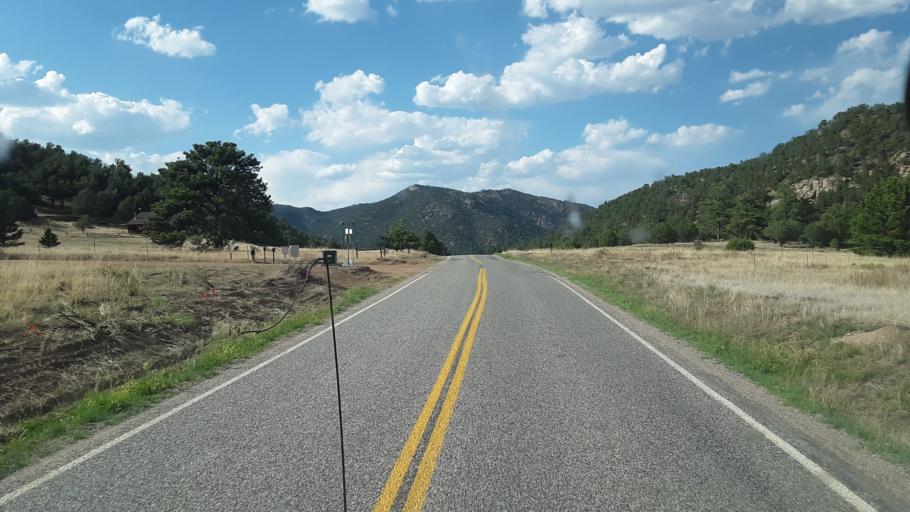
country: US
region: Colorado
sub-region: Fremont County
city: Canon City
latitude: 38.3735
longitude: -105.4566
